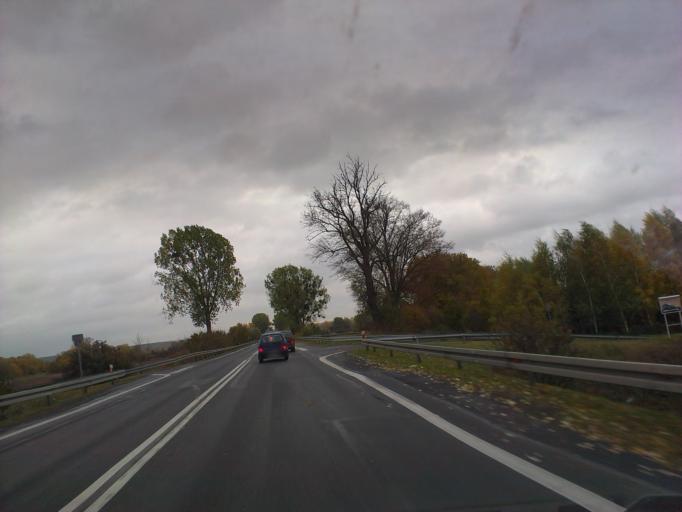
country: PL
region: Kujawsko-Pomorskie
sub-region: Powiat chelminski
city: Chelmno
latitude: 53.3814
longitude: 18.4158
